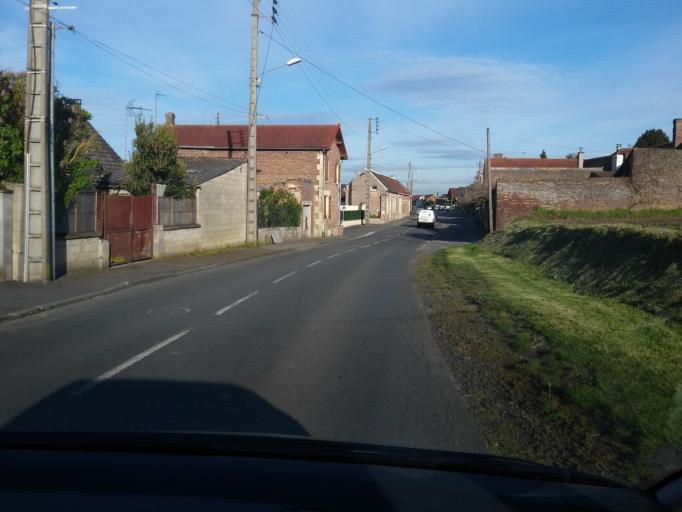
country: FR
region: Picardie
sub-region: Departement de l'Oise
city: Chevrieres
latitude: 49.3470
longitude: 2.6933
